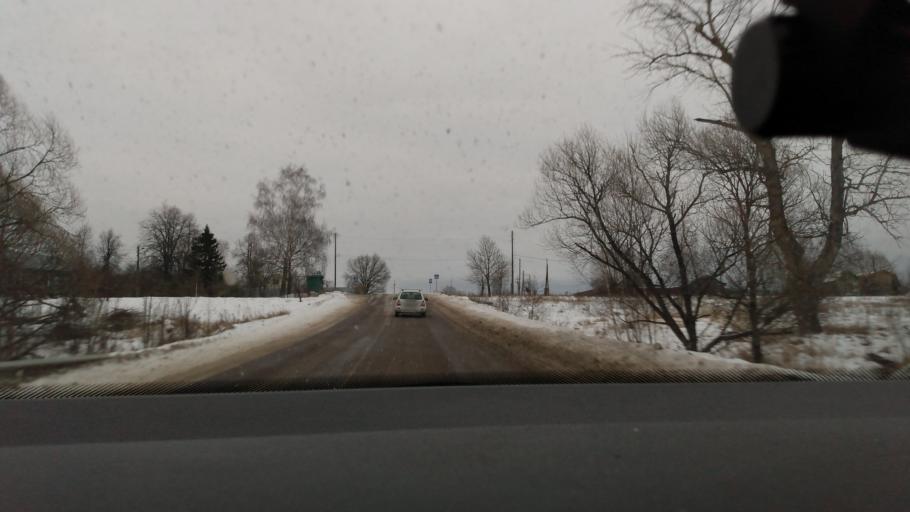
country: RU
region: Moskovskaya
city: Krasnaya Poyma
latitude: 55.1678
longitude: 39.1789
